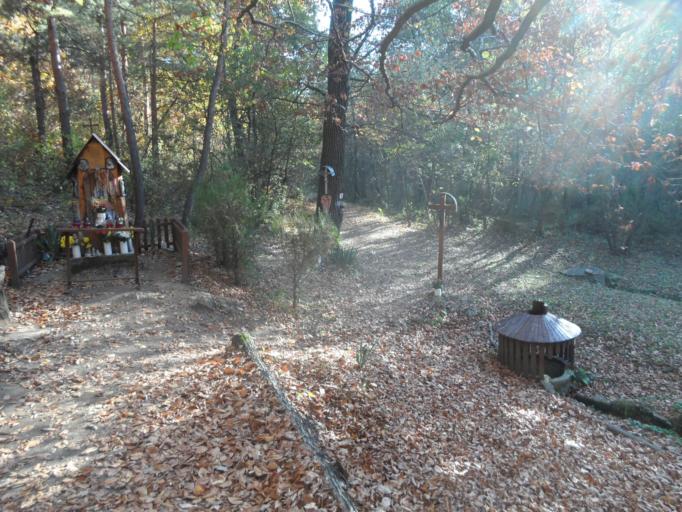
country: HU
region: Veszprem
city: Ajka
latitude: 47.1879
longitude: 17.5448
